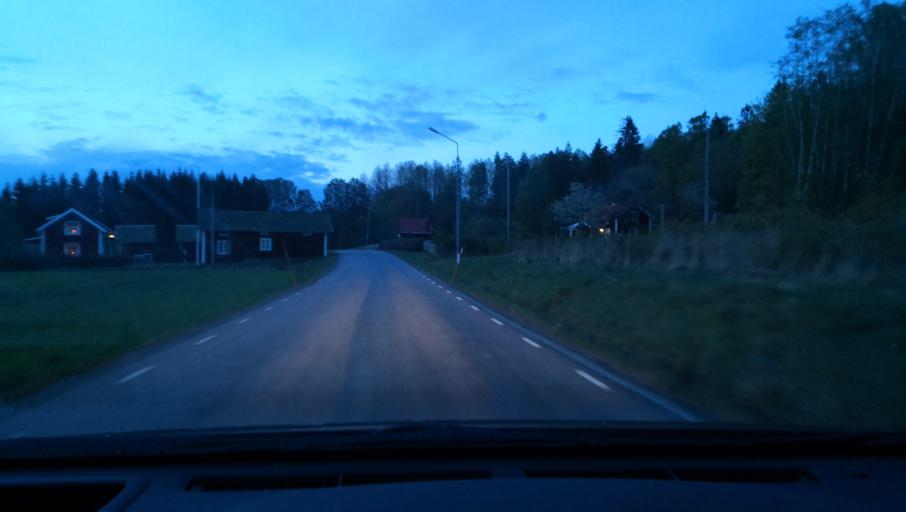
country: SE
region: OErebro
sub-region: Askersunds Kommun
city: Asbro
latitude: 59.0743
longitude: 15.0066
